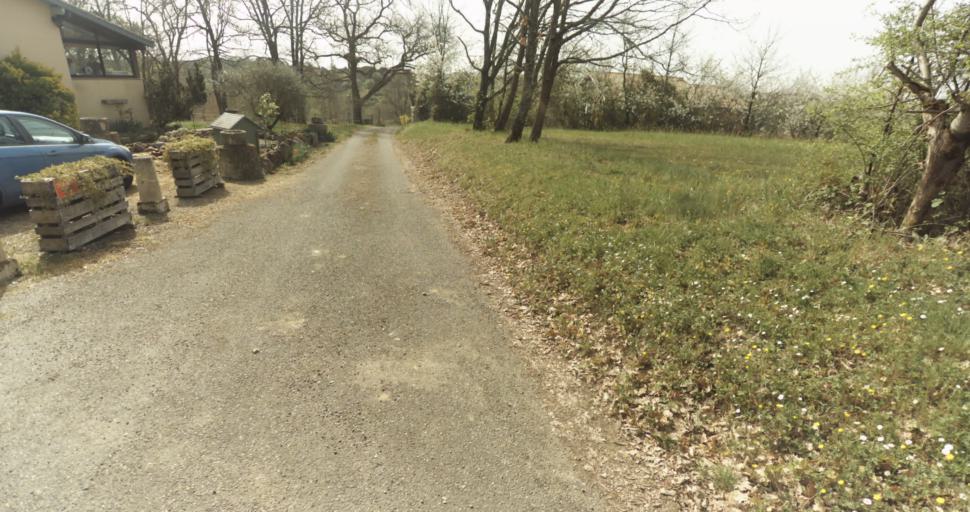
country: FR
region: Midi-Pyrenees
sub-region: Departement du Tarn-et-Garonne
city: Moissac
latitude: 44.1197
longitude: 1.0798
